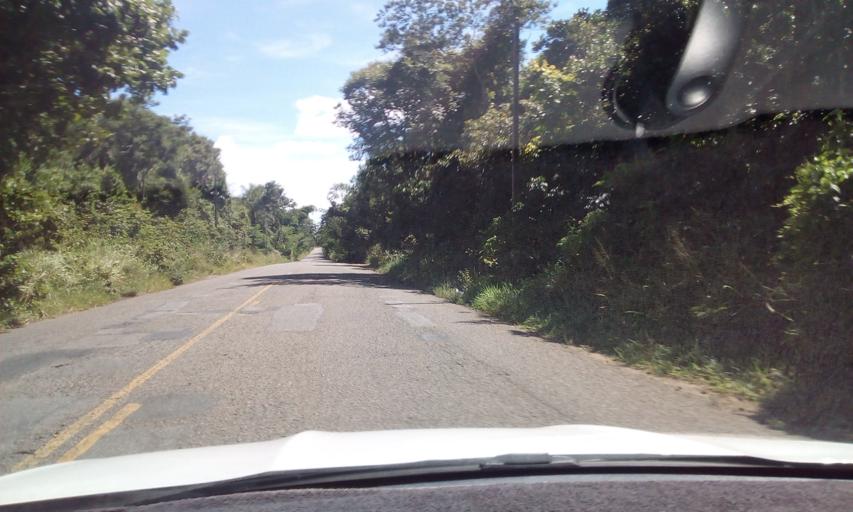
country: BR
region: Paraiba
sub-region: Areia
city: Remigio
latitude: -6.9667
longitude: -35.7396
